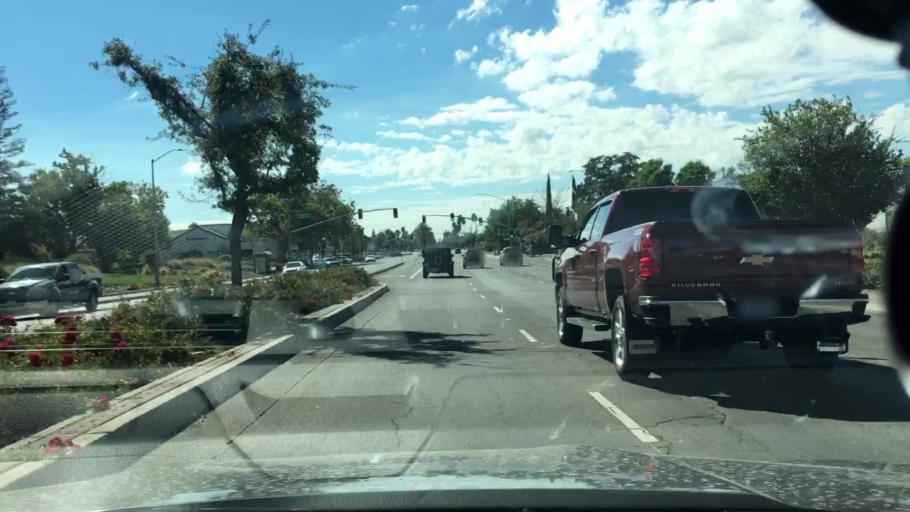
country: US
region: California
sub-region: Sacramento County
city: Arden-Arcade
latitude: 38.6153
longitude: -121.3830
